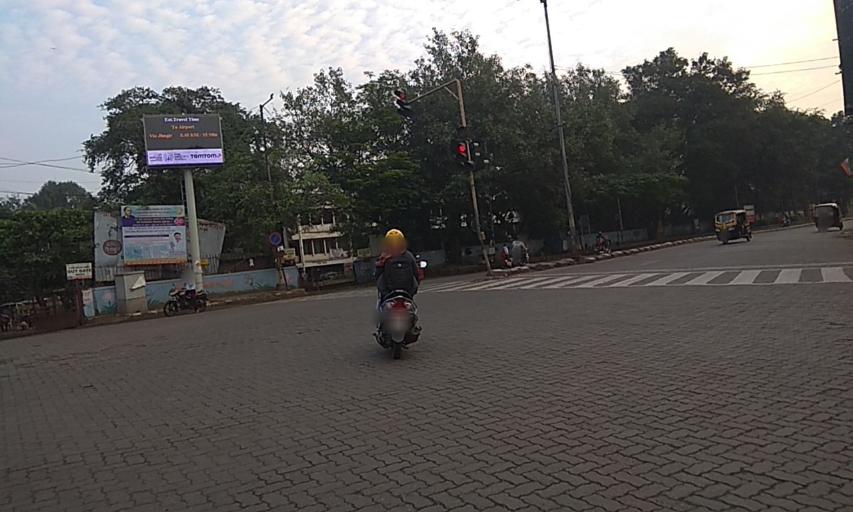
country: IN
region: Maharashtra
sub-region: Pune Division
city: Shivaji Nagar
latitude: 18.5297
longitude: 73.8633
